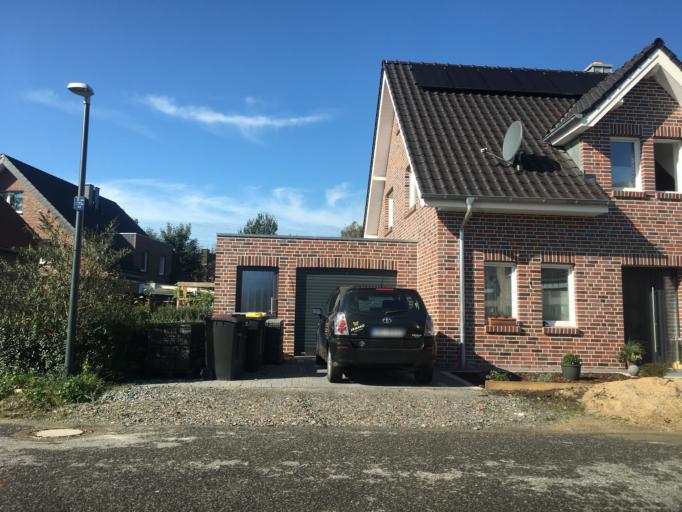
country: DE
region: North Rhine-Westphalia
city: Ludinghausen
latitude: 51.7794
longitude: 7.4602
